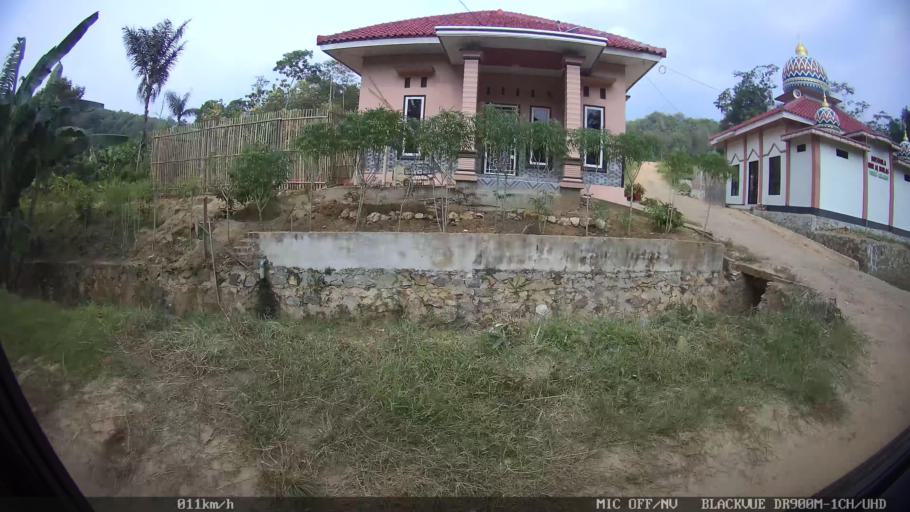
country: ID
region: Lampung
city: Gadingrejo
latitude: -5.3935
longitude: 105.0237
